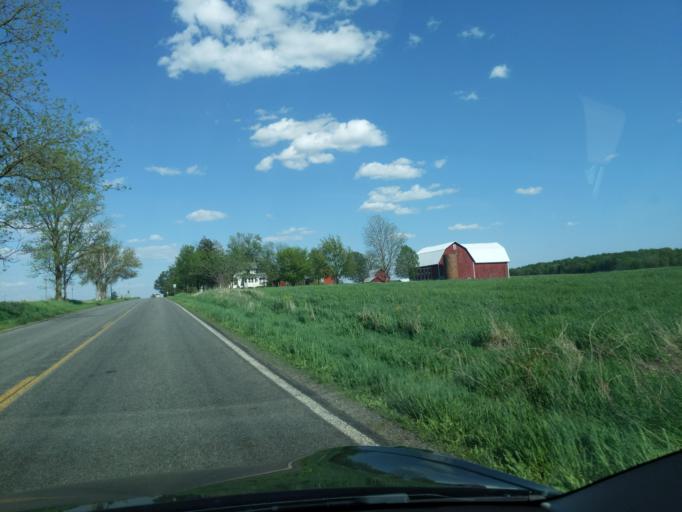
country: US
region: Michigan
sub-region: Ionia County
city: Lake Odessa
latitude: 42.7841
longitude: -85.2154
